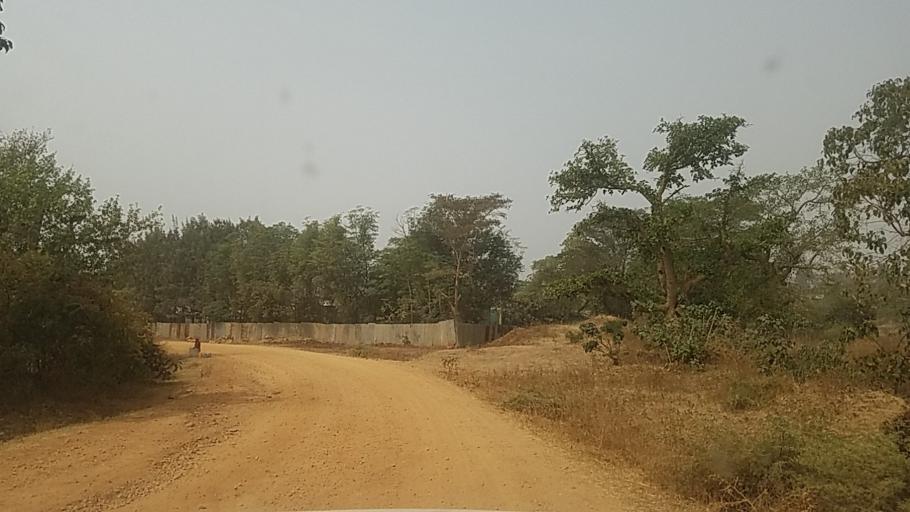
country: ET
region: Amhara
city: Bure
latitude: 10.7808
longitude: 36.2724
